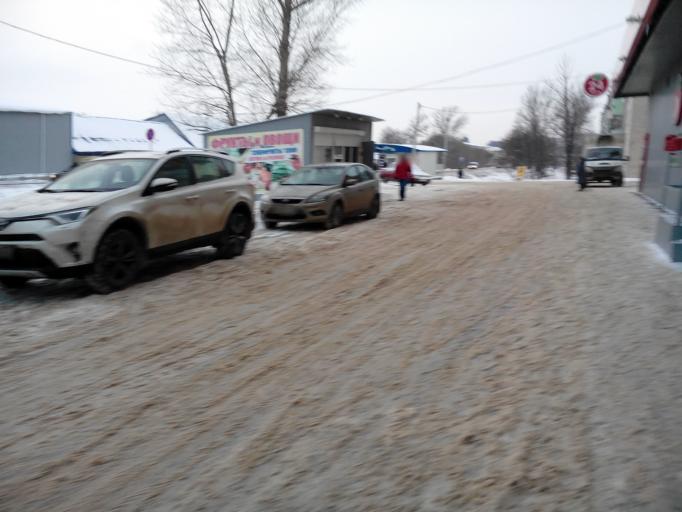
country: RU
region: Tula
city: Yefremov
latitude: 53.1497
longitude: 38.0773
